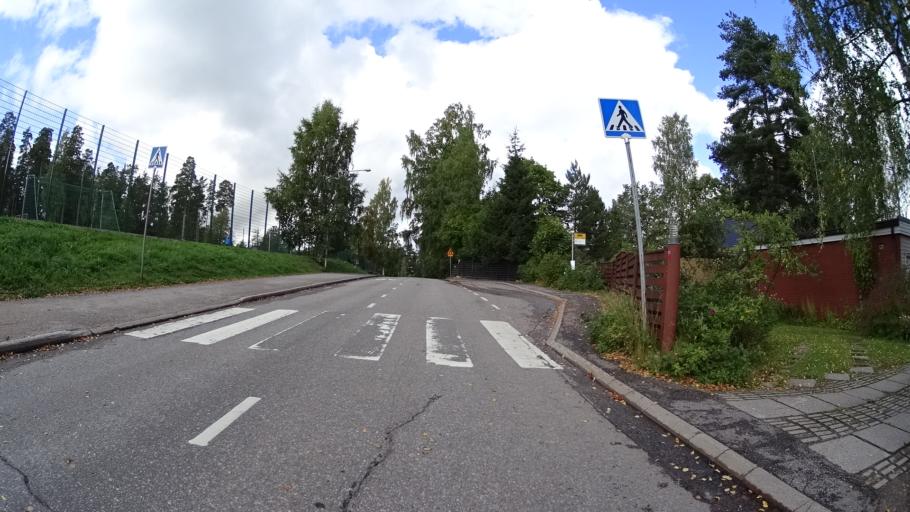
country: FI
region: Uusimaa
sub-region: Helsinki
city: Kilo
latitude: 60.2464
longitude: 24.7696
